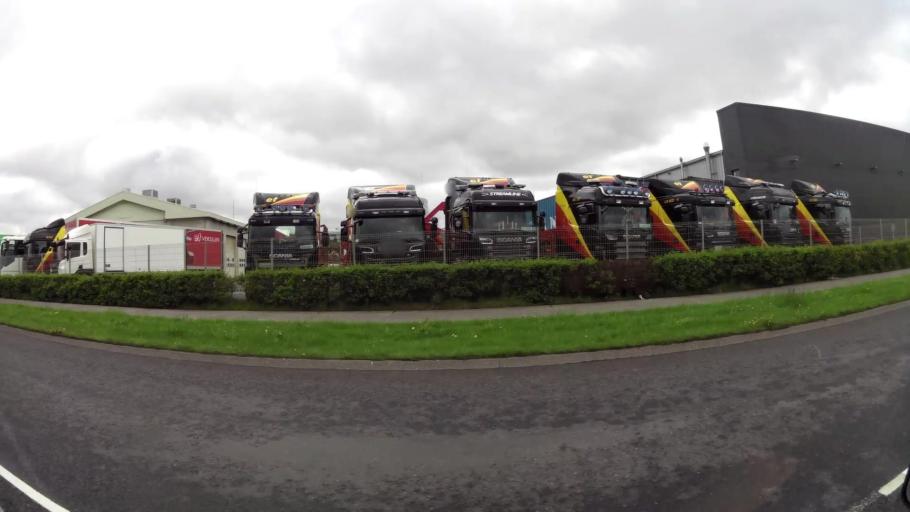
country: IS
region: Capital Region
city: Reykjavik
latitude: 64.1531
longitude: -21.8677
